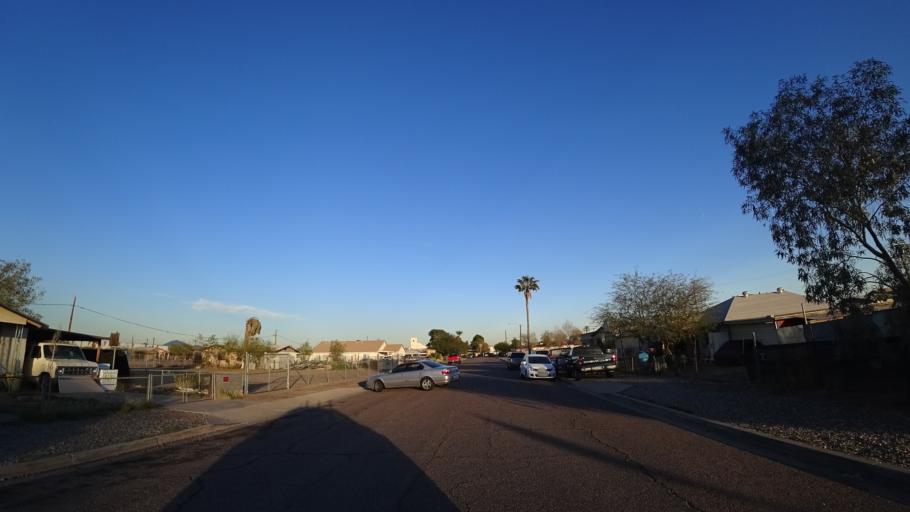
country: US
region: Arizona
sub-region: Maricopa County
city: Phoenix
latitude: 33.4340
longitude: -112.0585
